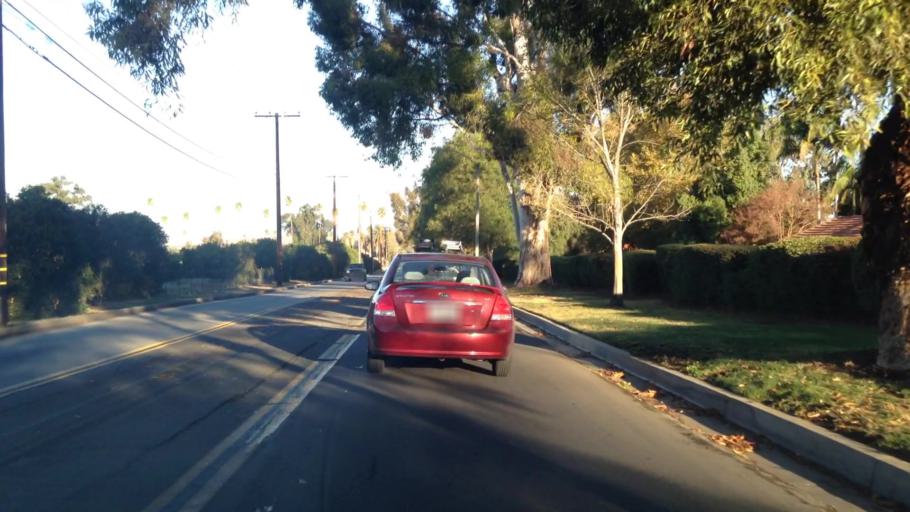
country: US
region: California
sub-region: Riverside County
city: Riverside
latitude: 33.9275
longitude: -117.3871
